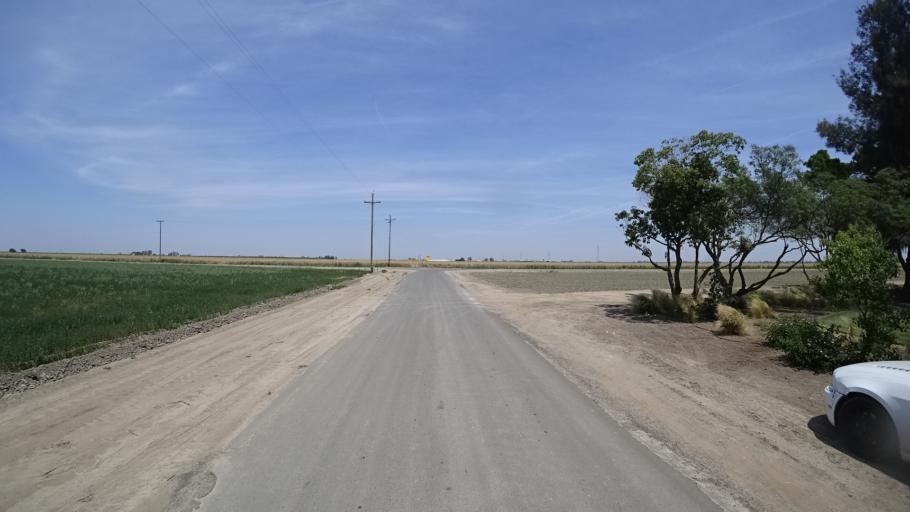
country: US
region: California
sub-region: Fresno County
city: Riverdale
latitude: 36.4049
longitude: -119.8955
